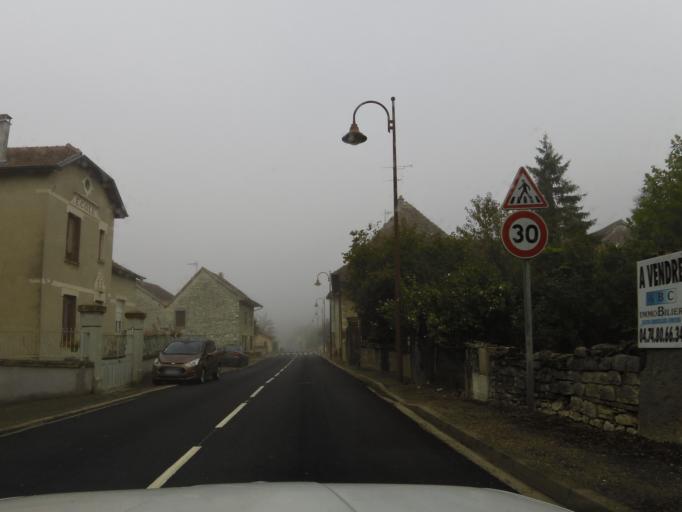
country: FR
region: Rhone-Alpes
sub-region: Departement de l'Isere
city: Creys-Mepieu
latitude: 45.7637
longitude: 5.4819
